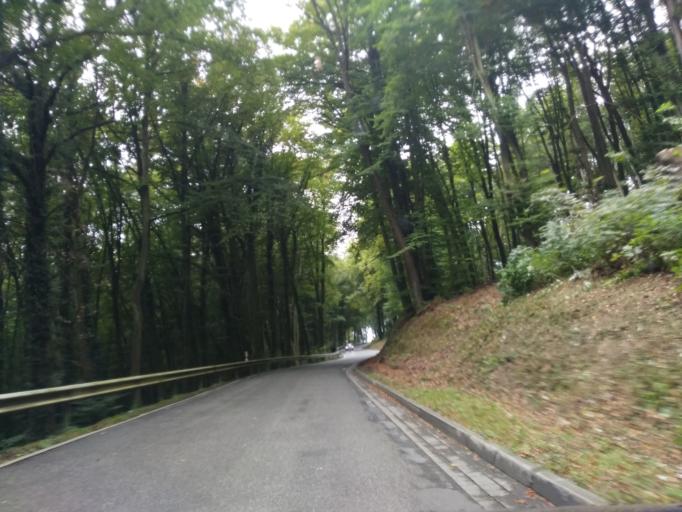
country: DE
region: Rheinland-Pfalz
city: Kasbach-Ohlenberg
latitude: 50.6046
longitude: 7.2775
